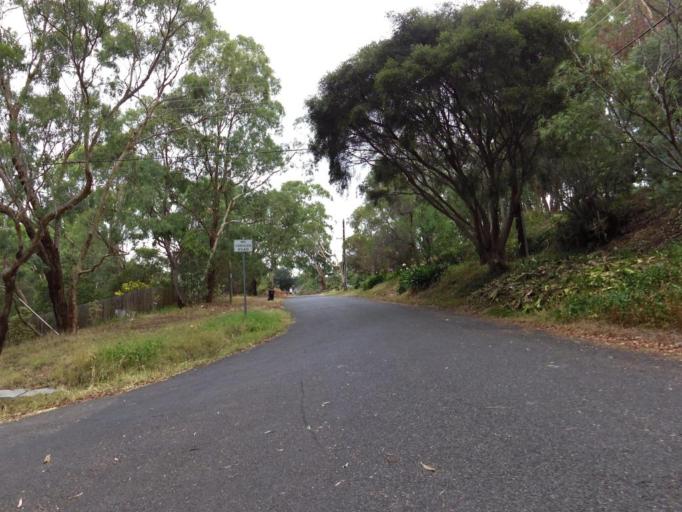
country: AU
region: Victoria
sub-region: Manningham
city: Templestowe Lower
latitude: -37.7652
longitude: 145.1273
